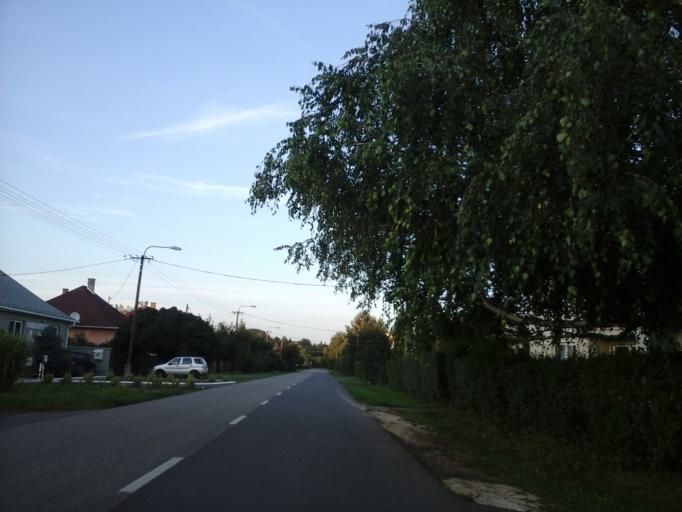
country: HU
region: Hajdu-Bihar
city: Hajduszoboszlo
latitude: 47.4598
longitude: 21.4130
